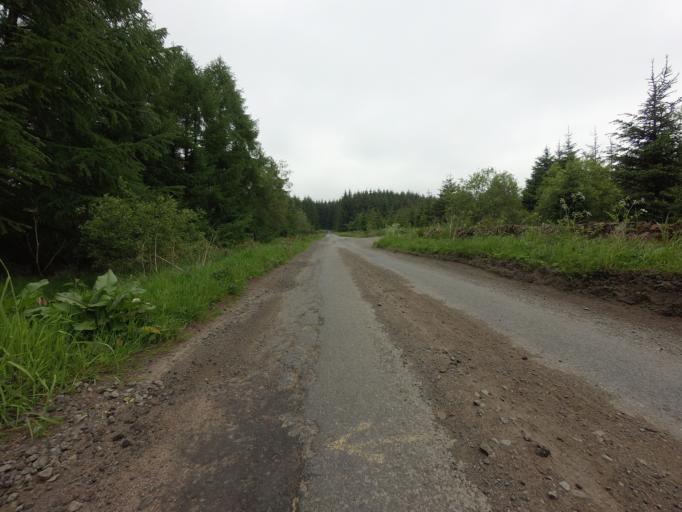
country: GB
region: Scotland
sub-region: Fife
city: Townhill
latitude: 56.1393
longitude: -3.4449
